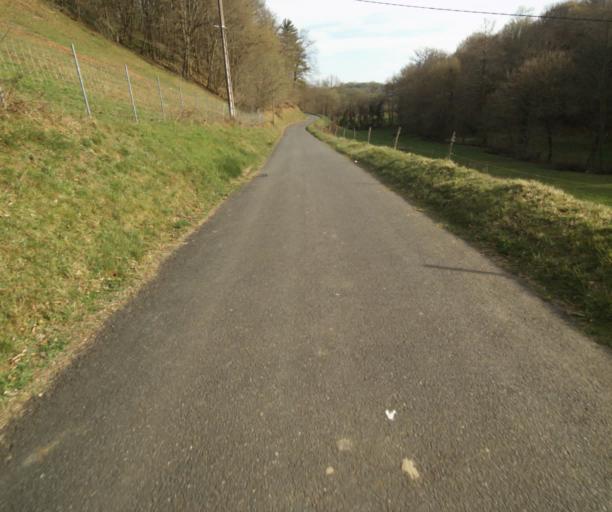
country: FR
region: Limousin
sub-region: Departement de la Correze
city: Naves
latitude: 45.2966
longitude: 1.7558
